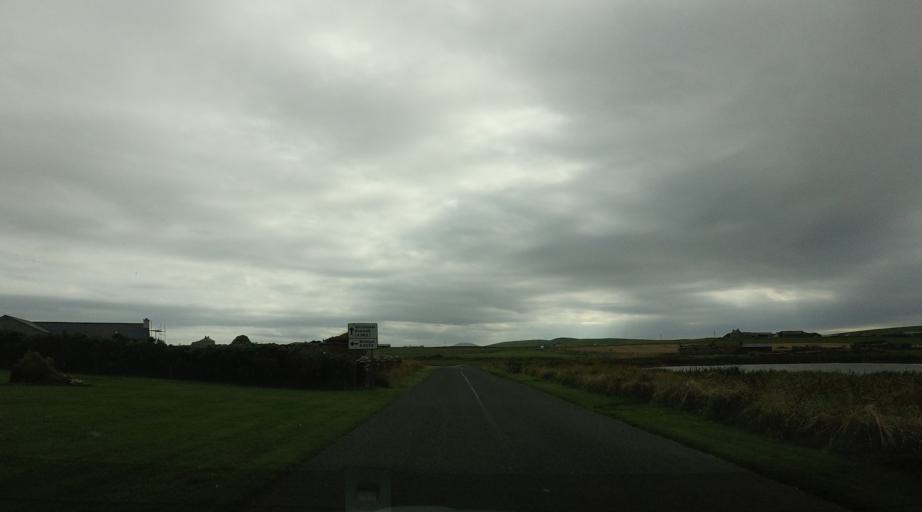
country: GB
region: Scotland
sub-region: Orkney Islands
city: Stromness
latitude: 59.0411
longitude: -3.3097
